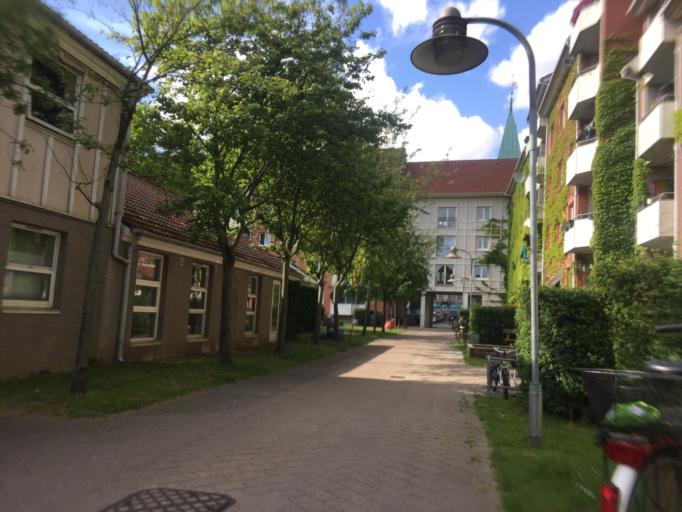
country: DK
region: Capital Region
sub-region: Kobenhavn
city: Copenhagen
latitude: 55.6708
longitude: 12.5508
